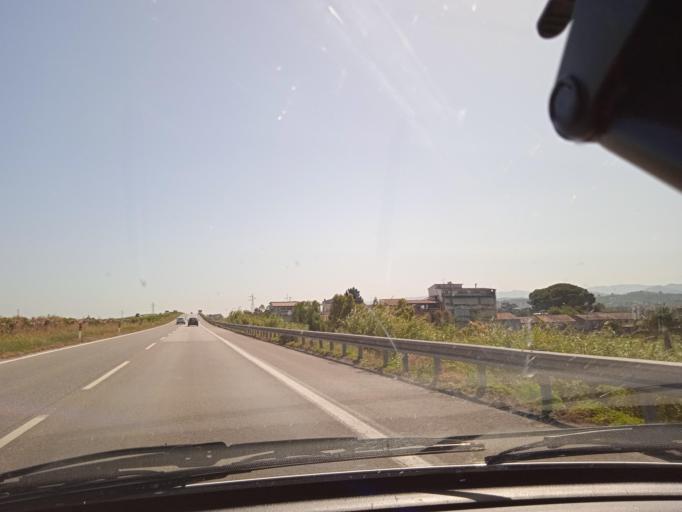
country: IT
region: Sicily
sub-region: Messina
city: Barcellona Pozzo di Gotto
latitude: 38.1685
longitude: 15.2209
